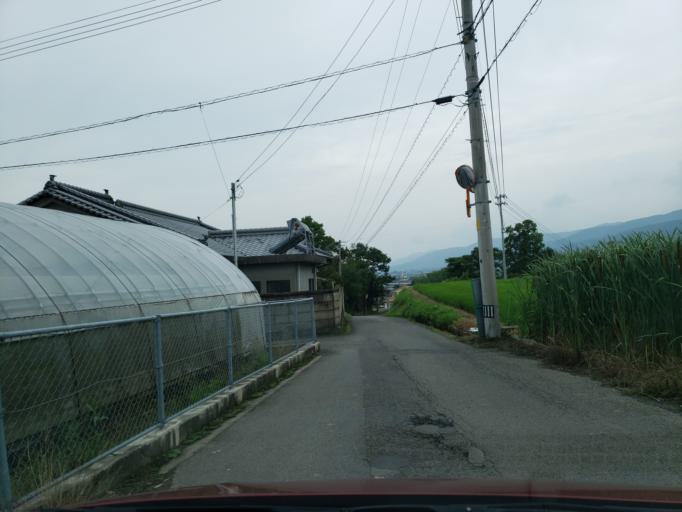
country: JP
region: Tokushima
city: Kamojimacho-jogejima
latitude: 34.0989
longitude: 134.2841
